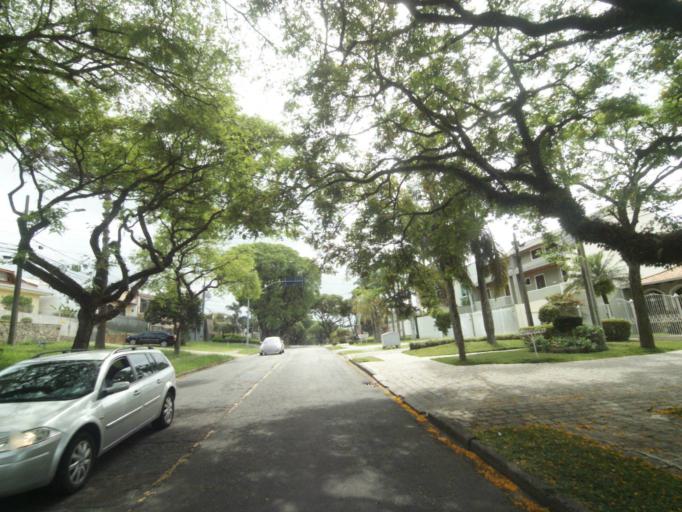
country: BR
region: Parana
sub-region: Curitiba
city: Curitiba
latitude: -25.4251
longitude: -49.2340
